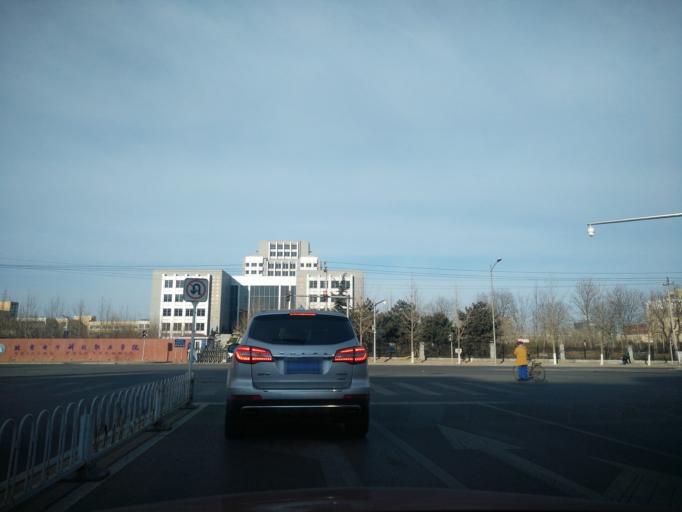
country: CN
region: Beijing
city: Jiugong
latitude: 39.7676
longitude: 116.4999
